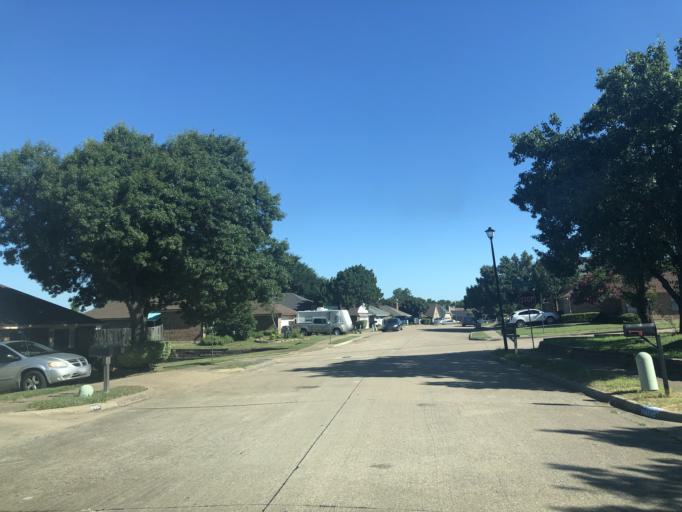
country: US
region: Texas
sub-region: Dallas County
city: Duncanville
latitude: 32.6654
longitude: -96.9350
